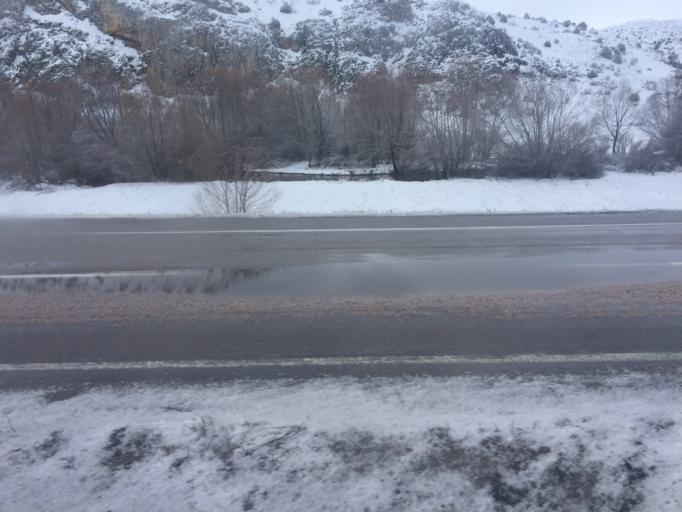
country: TR
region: Kayseri
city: Sariz
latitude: 38.3706
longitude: 36.4440
